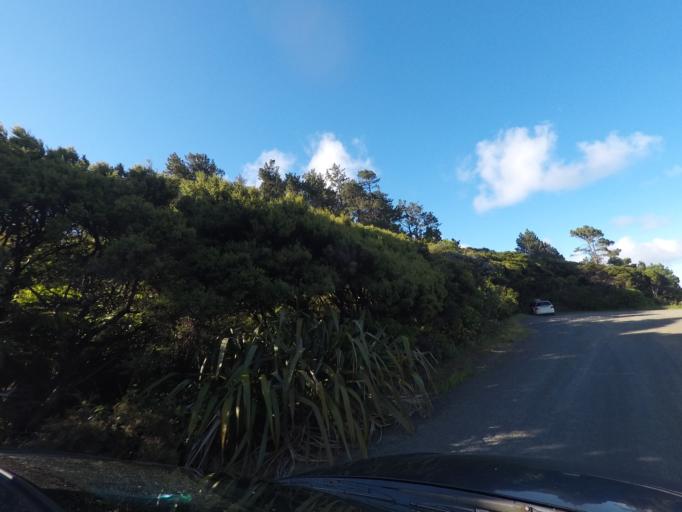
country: NZ
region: Auckland
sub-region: Auckland
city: Titirangi
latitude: -37.0153
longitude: 174.6031
